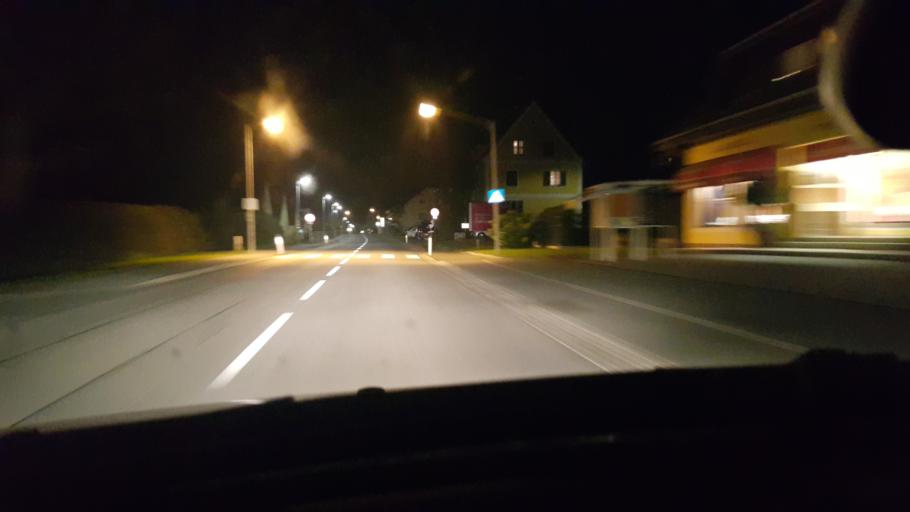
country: AT
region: Styria
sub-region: Politischer Bezirk Deutschlandsberg
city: Sankt Martin im Sulmtal
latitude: 46.7316
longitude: 15.3022
